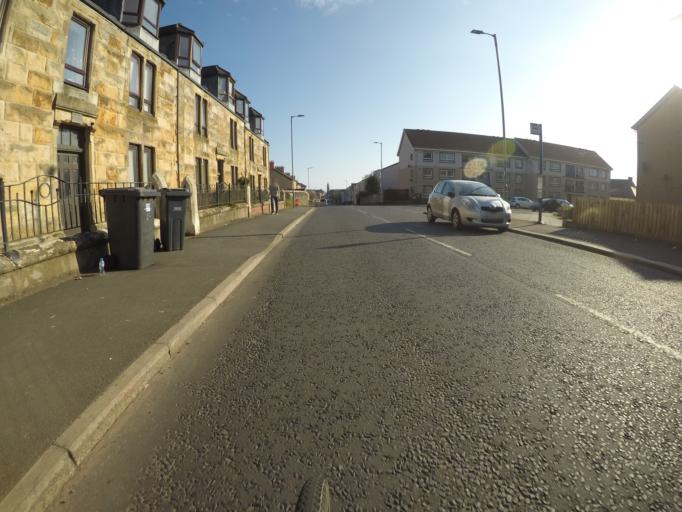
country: GB
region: Scotland
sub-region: North Ayrshire
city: Saltcoats
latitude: 55.6374
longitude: -4.7830
